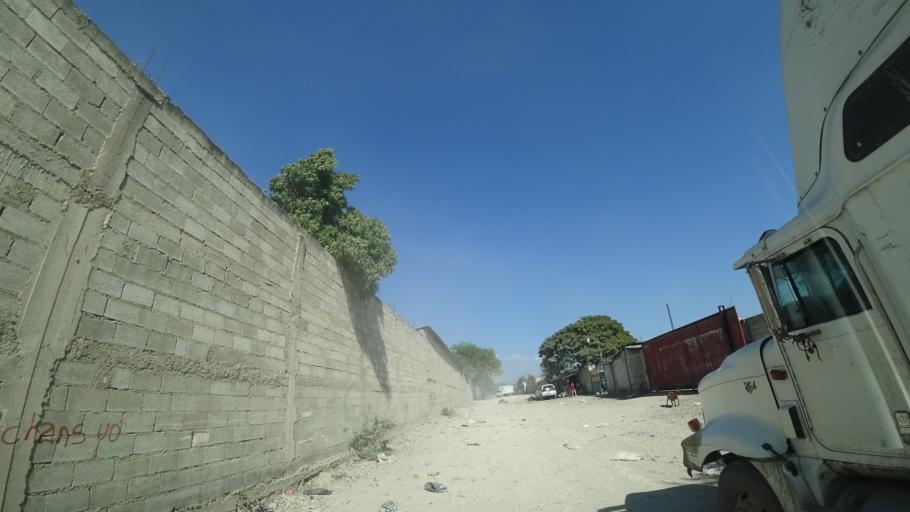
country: HT
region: Ouest
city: Delmas 73
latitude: 18.5807
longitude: -72.3159
